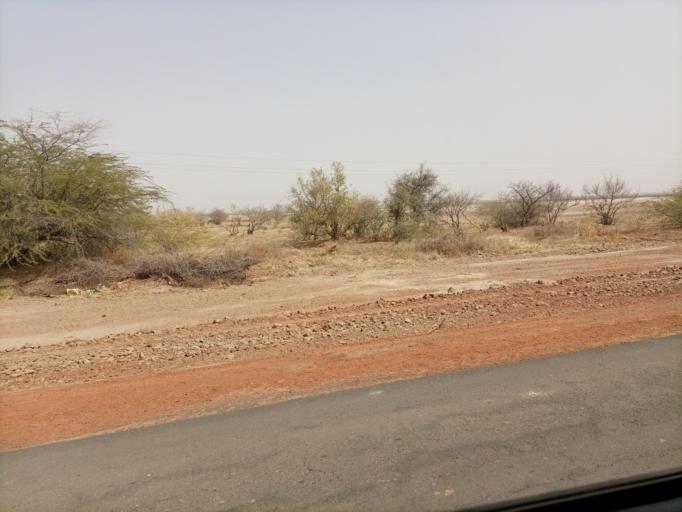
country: SN
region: Fatick
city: Foundiougne
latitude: 14.1569
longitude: -16.4690
